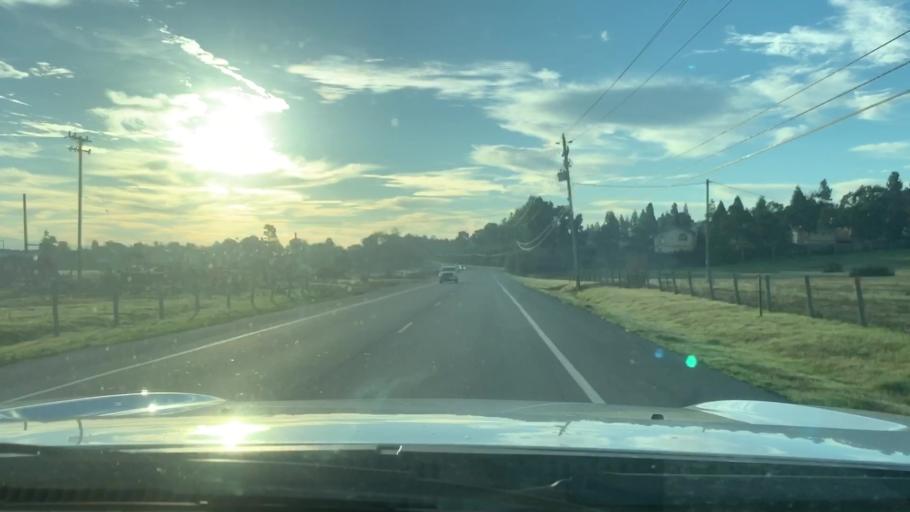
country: US
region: California
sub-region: San Luis Obispo County
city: San Luis Obispo
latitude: 35.2701
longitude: -120.7057
